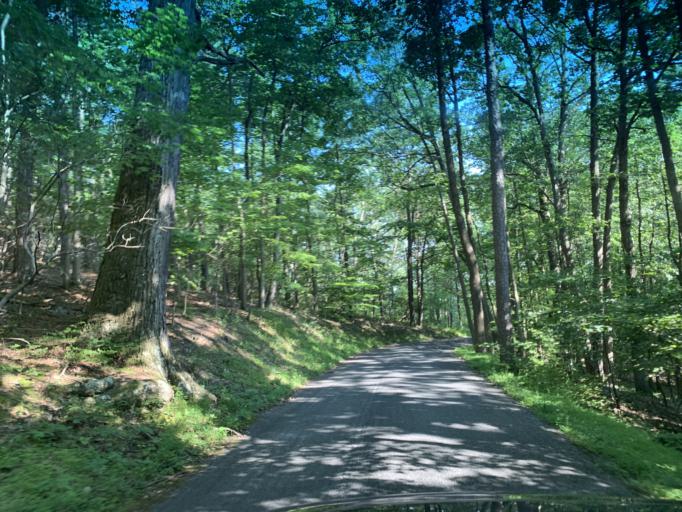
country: US
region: Maryland
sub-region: Frederick County
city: Urbana
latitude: 39.2583
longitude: -77.3953
